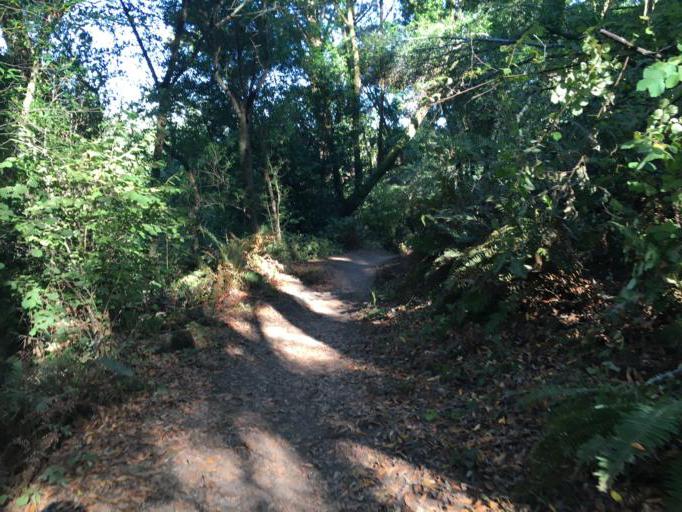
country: US
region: California
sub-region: Marin County
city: Inverness
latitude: 38.0378
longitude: -122.8070
